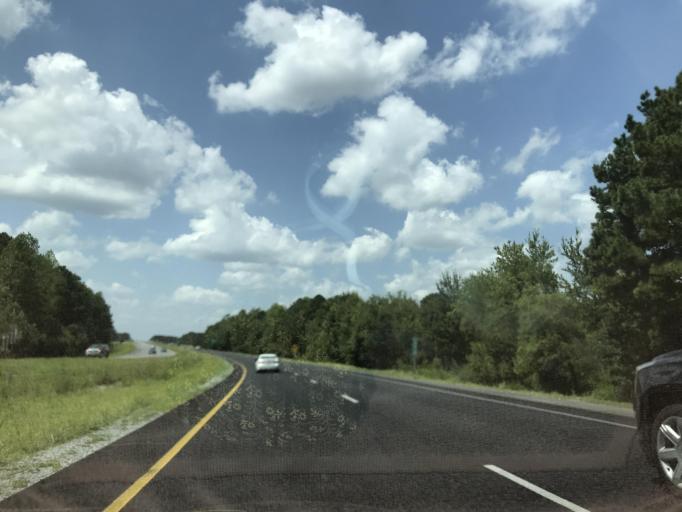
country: US
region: North Carolina
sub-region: Duplin County
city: Warsaw
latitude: 34.9441
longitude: -78.0631
